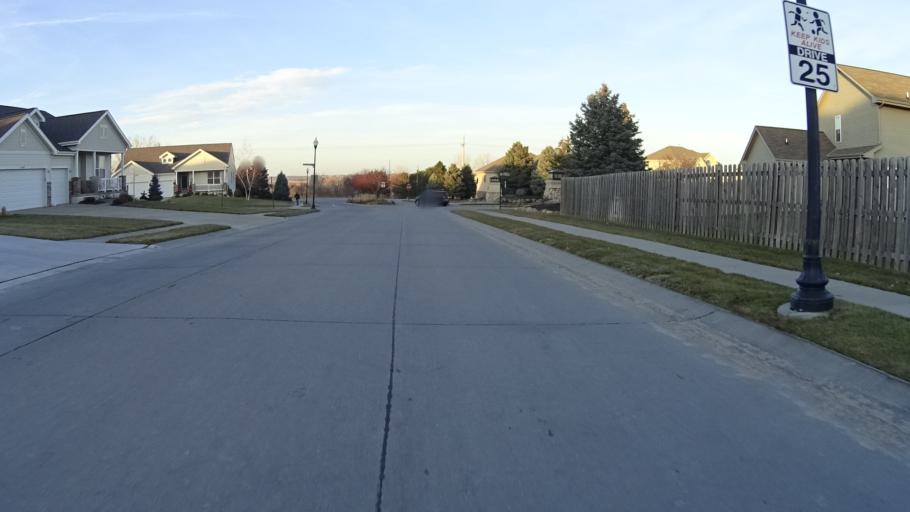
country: US
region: Nebraska
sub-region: Sarpy County
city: Papillion
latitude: 41.1317
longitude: -96.0690
